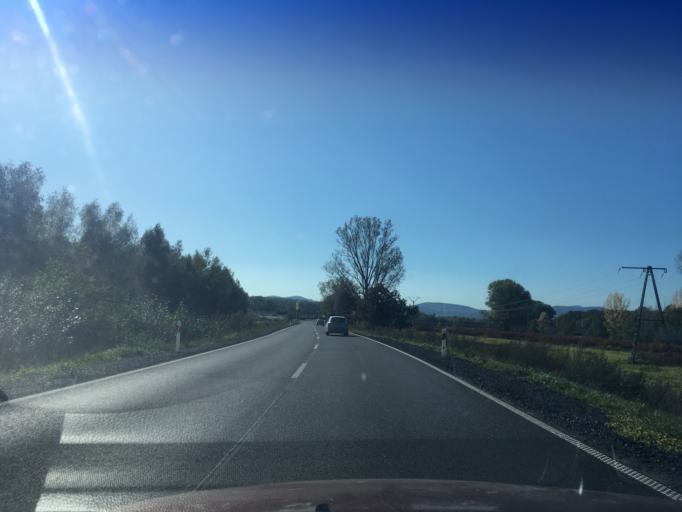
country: DE
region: Saxony
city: Zittau
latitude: 50.9045
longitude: 14.8470
